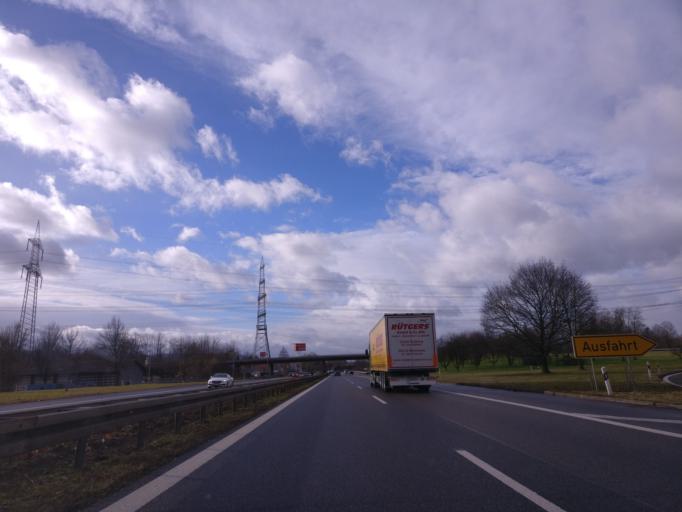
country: DE
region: Baden-Wuerttemberg
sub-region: Regierungsbezirk Stuttgart
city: Weinstadt-Endersbach
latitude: 48.8152
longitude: 9.3822
